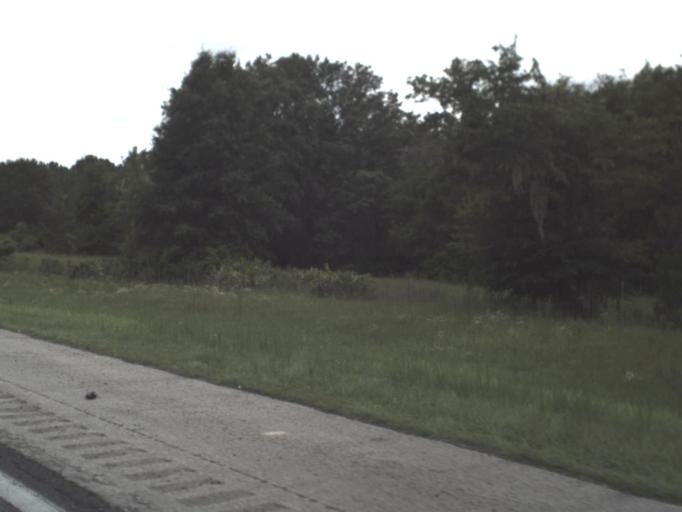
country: US
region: Florida
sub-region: Alachua County
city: High Springs
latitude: 29.9122
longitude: -82.5526
